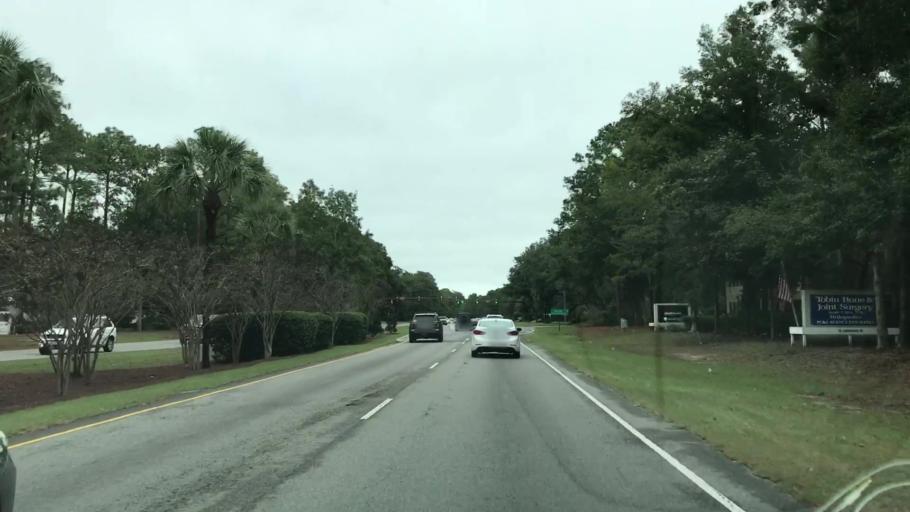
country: US
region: South Carolina
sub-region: Beaufort County
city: Hilton Head Island
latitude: 32.2137
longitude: -80.7224
